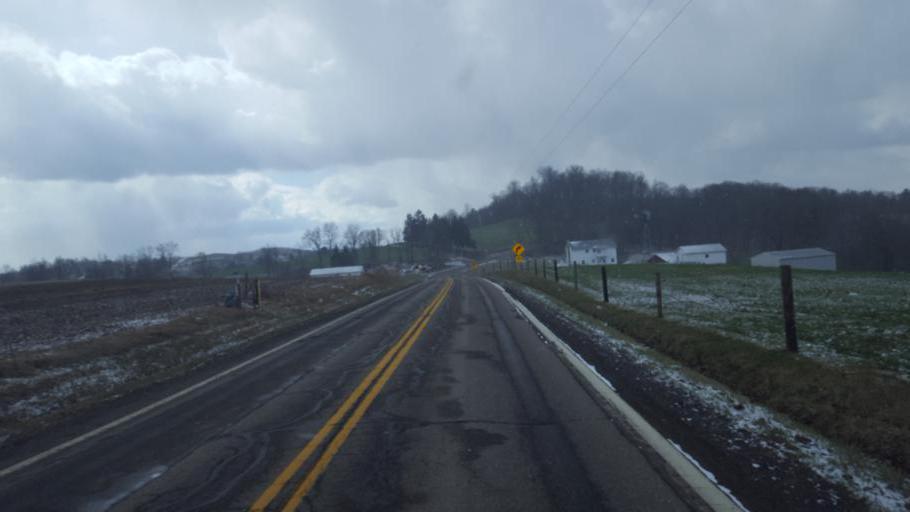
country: US
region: Ohio
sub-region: Coshocton County
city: West Lafayette
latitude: 40.4274
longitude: -81.7875
